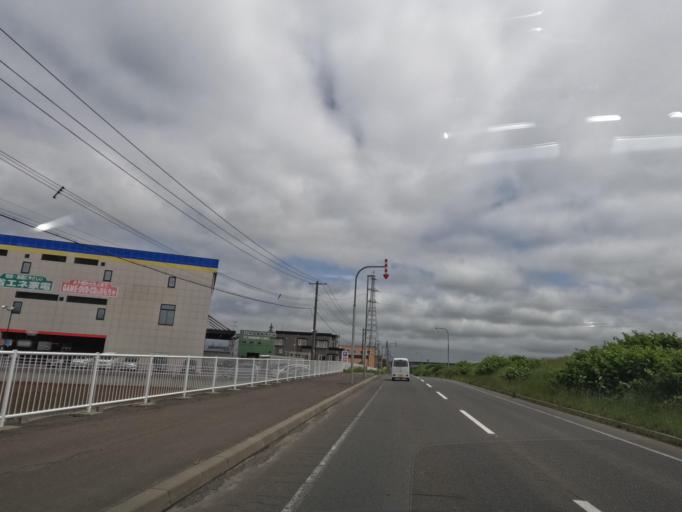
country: JP
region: Hokkaido
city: Sapporo
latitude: 43.0792
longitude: 141.4074
